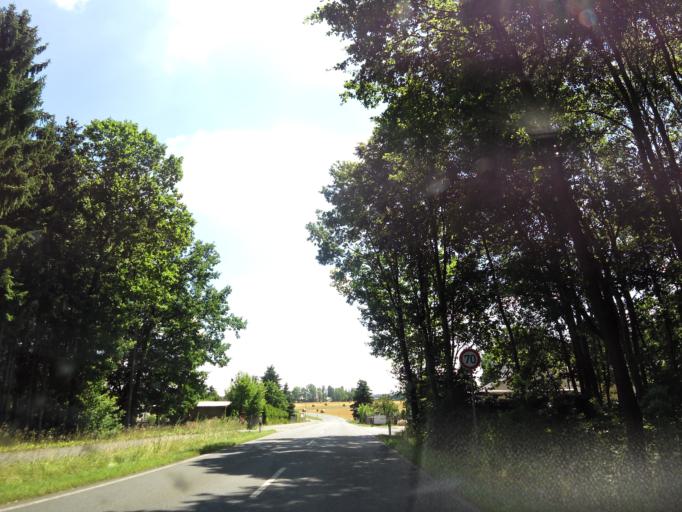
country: DE
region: Thuringia
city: Reichenbach
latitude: 50.8868
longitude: 11.8835
